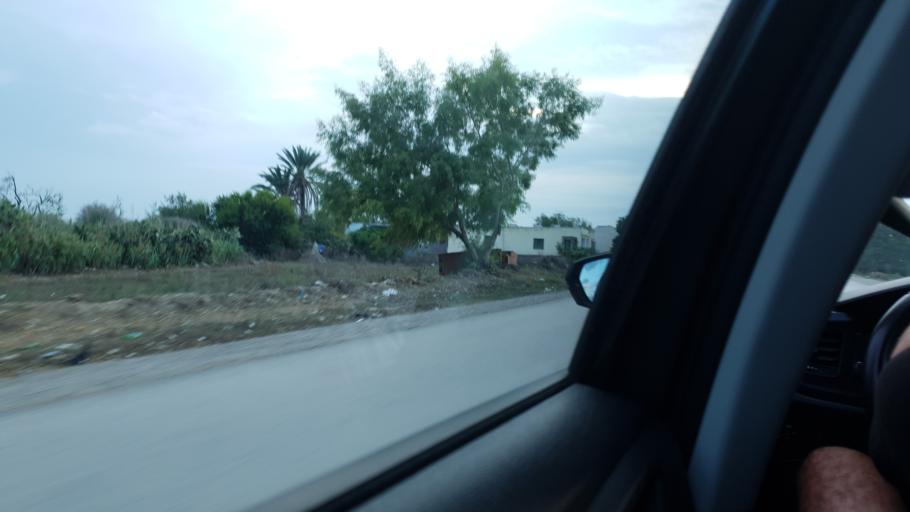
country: TN
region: Banzart
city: Al `Aliyah
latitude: 37.1304
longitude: 10.0683
